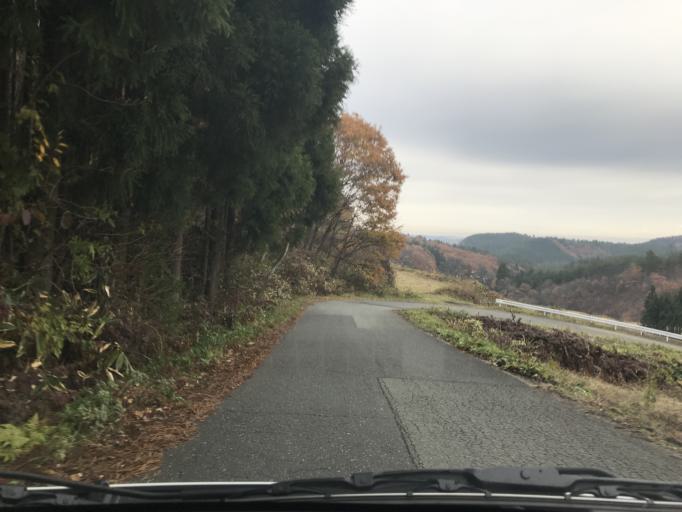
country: JP
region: Iwate
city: Ichinoseki
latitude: 39.0002
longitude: 141.0260
